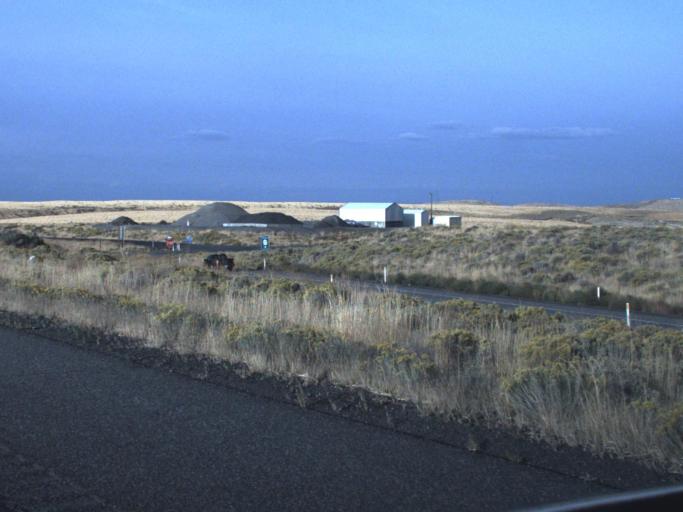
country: US
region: Washington
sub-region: Benton County
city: Highland
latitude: 46.1413
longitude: -119.2018
